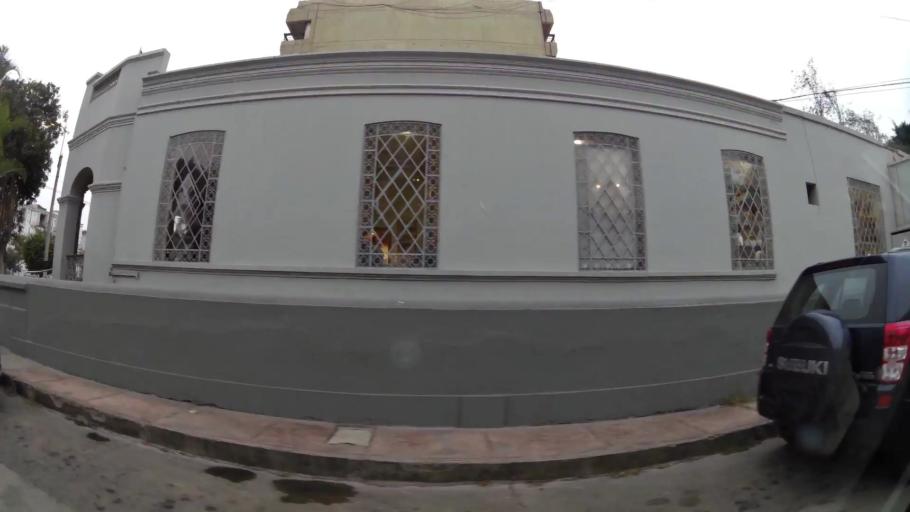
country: PE
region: Lima
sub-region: Lima
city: Surco
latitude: -12.1438
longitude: -77.0240
